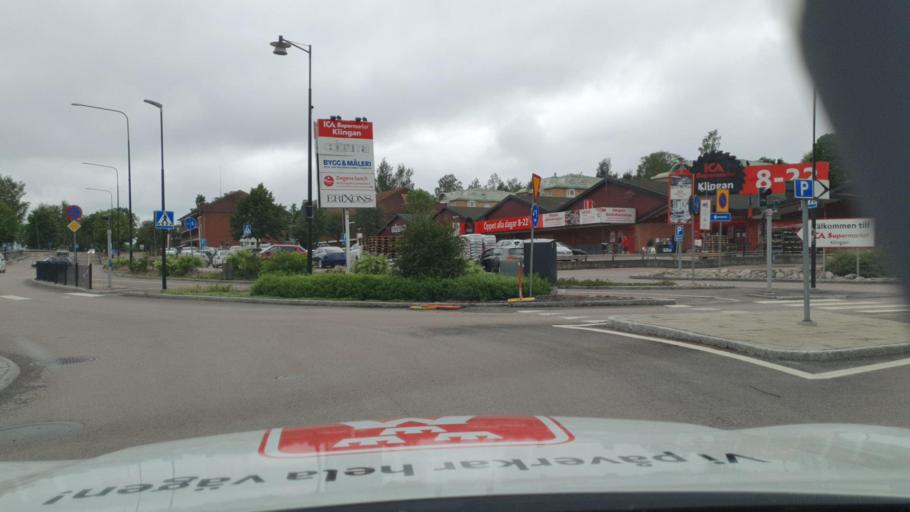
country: SE
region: Vaermland
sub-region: Grums Kommun
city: Grums
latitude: 59.3529
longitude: 13.1125
